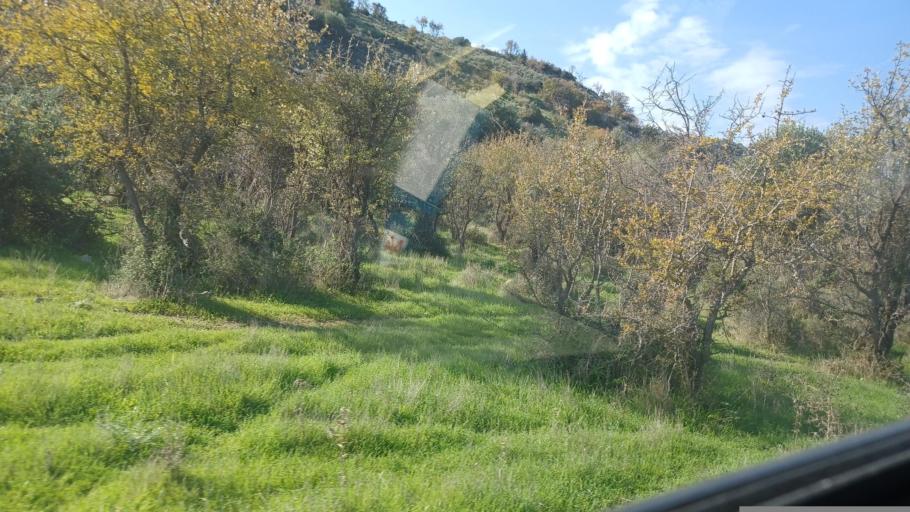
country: CY
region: Pafos
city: Mesogi
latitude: 34.7644
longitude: 32.5745
